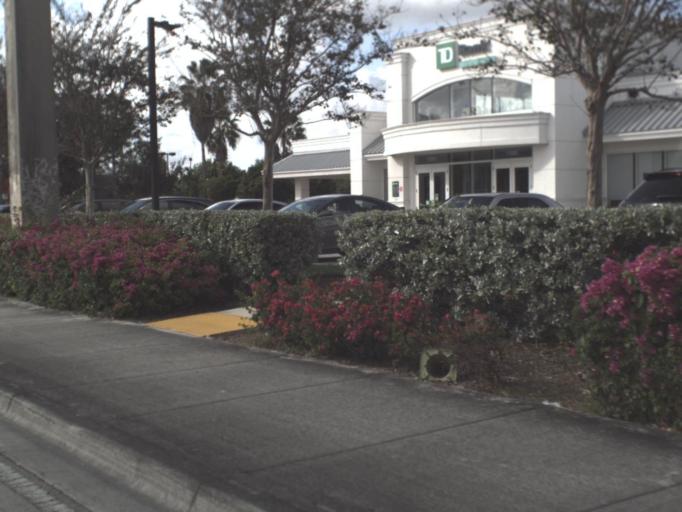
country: US
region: Florida
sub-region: Miami-Dade County
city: Richmond Heights
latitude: 25.6273
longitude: -80.3856
